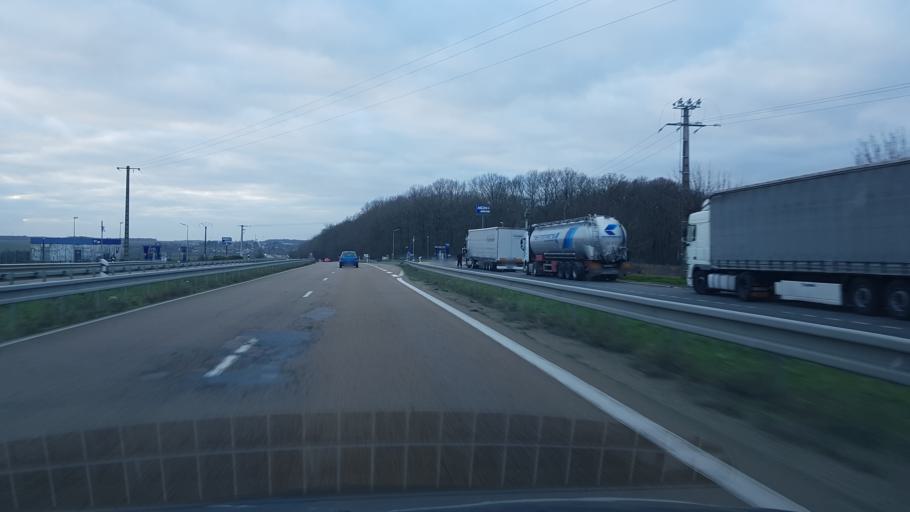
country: FR
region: Champagne-Ardenne
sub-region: Departement de la Marne
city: Esternay
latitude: 48.7310
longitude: 3.5846
